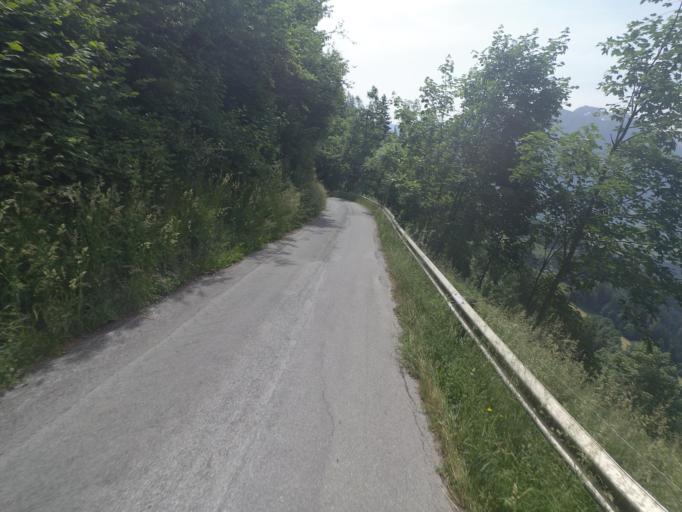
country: AT
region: Salzburg
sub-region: Politischer Bezirk Sankt Johann im Pongau
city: Muhlbach am Hochkonig
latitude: 47.3452
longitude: 13.1245
